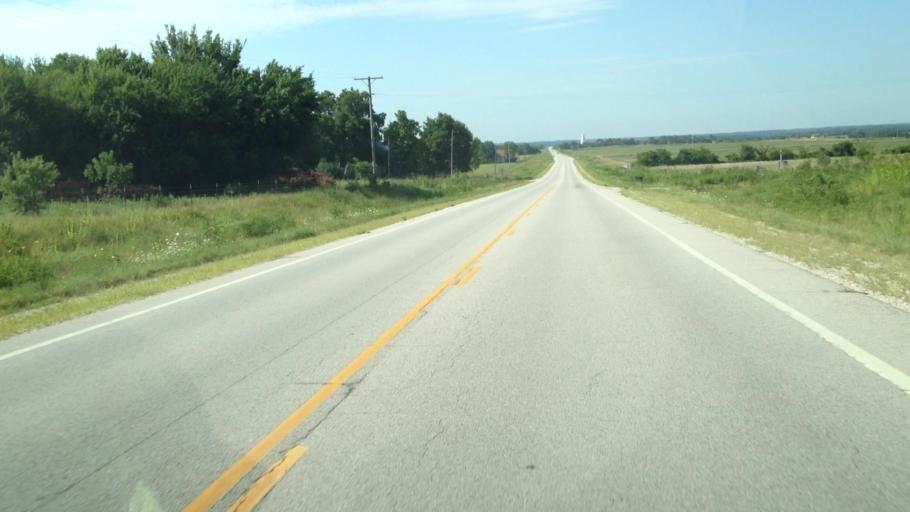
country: US
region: Kansas
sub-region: Neosho County
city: Erie
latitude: 37.4797
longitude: -95.2693
